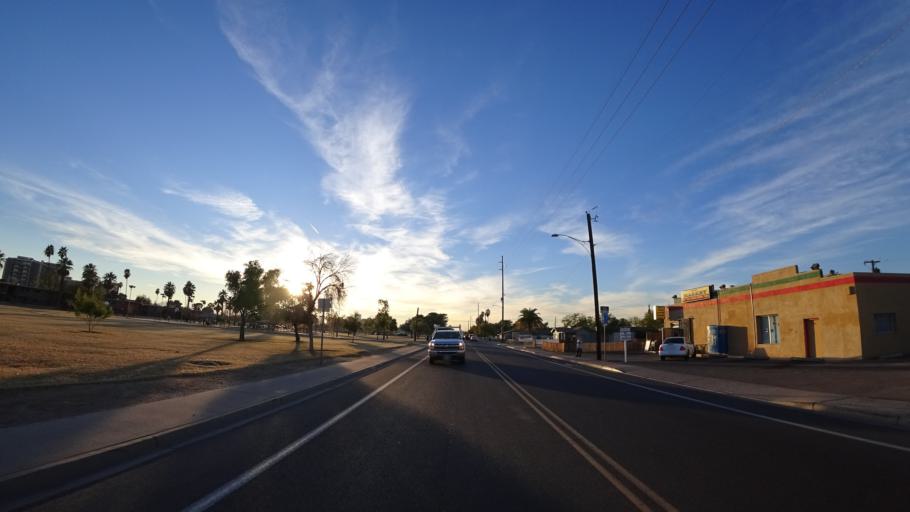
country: US
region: Arizona
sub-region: Maricopa County
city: Phoenix
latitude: 33.4586
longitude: -112.0394
